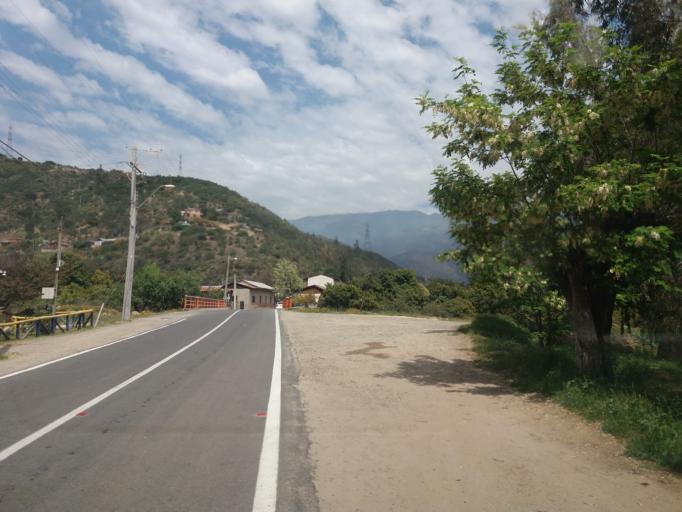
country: CL
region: Valparaiso
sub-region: Provincia de Marga Marga
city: Limache
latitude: -33.0493
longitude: -71.1001
